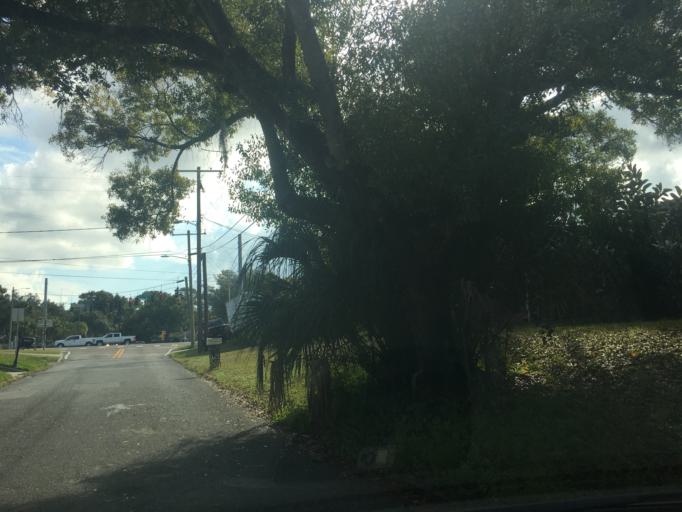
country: US
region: Florida
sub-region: Hillsborough County
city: Egypt Lake-Leto
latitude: 27.9968
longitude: -82.4700
